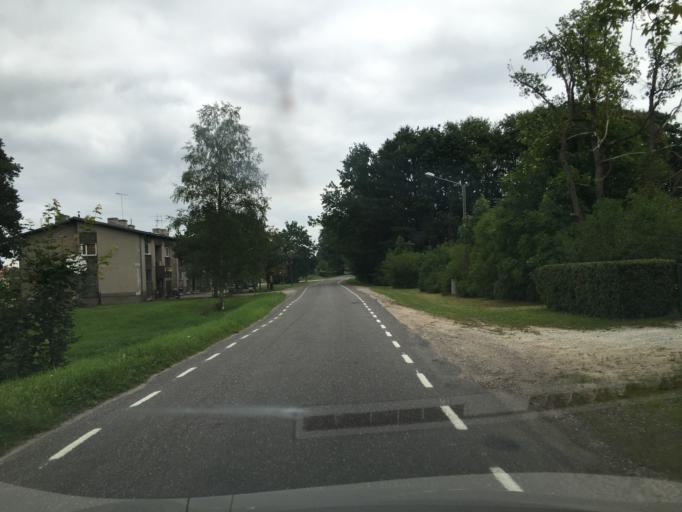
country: EE
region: Raplamaa
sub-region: Kehtna vald
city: Kehtna
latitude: 58.8607
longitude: 25.0006
